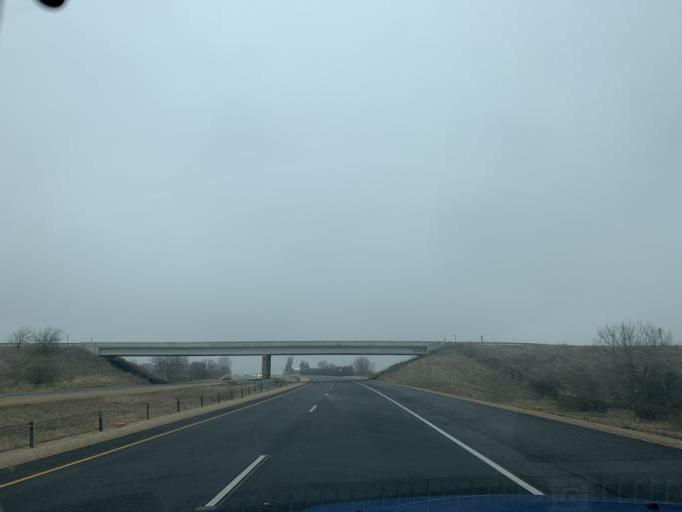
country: US
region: Wisconsin
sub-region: Dane County
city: Sun Prairie
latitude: 43.2108
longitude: -89.1709
